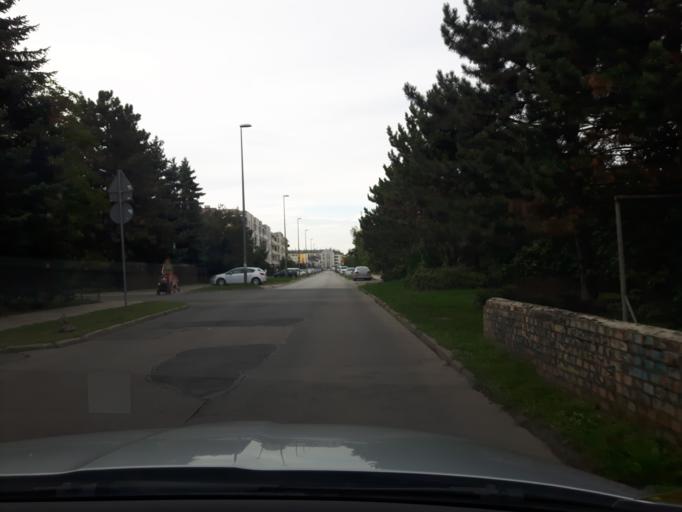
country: PL
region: Masovian Voivodeship
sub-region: Powiat wolominski
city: Zabki
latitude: 52.2822
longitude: 21.0834
